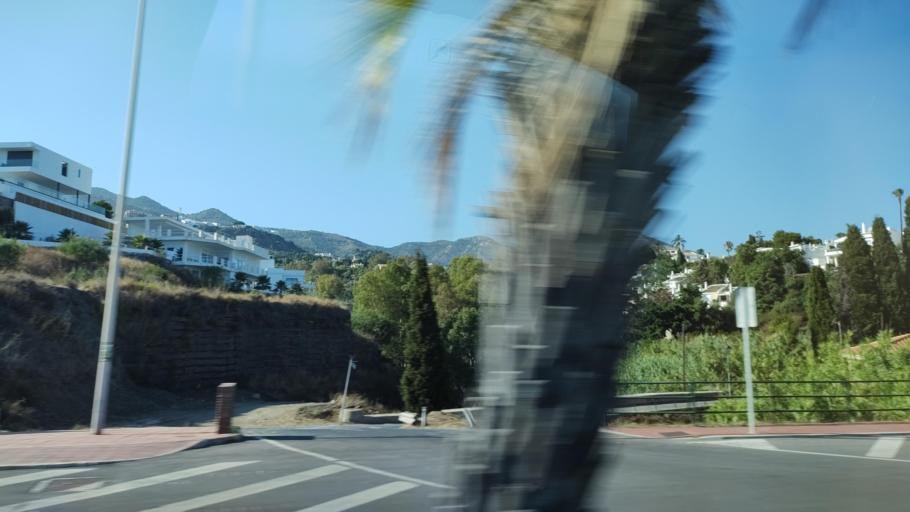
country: ES
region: Andalusia
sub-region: Provincia de Malaga
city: Benalmadena
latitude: 36.5778
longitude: -4.5700
